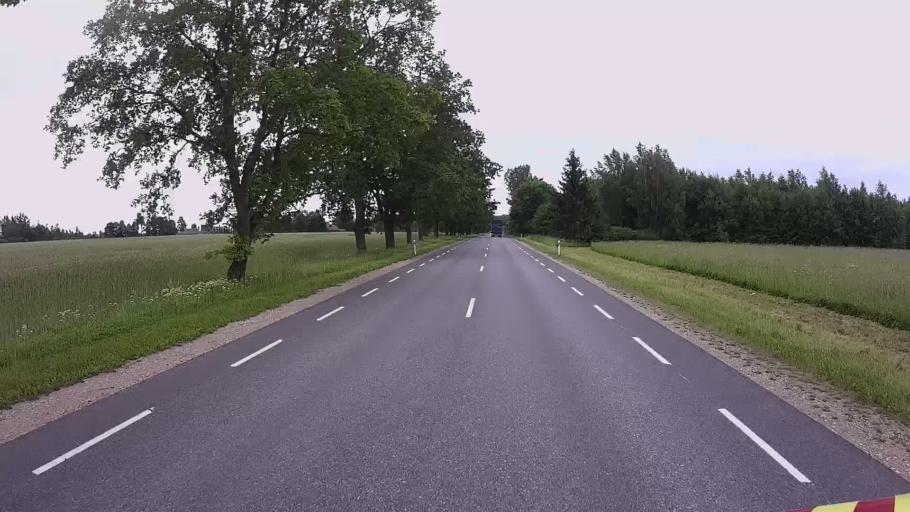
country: EE
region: Viljandimaa
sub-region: Karksi vald
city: Karksi-Nuia
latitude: 58.1241
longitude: 25.5826
